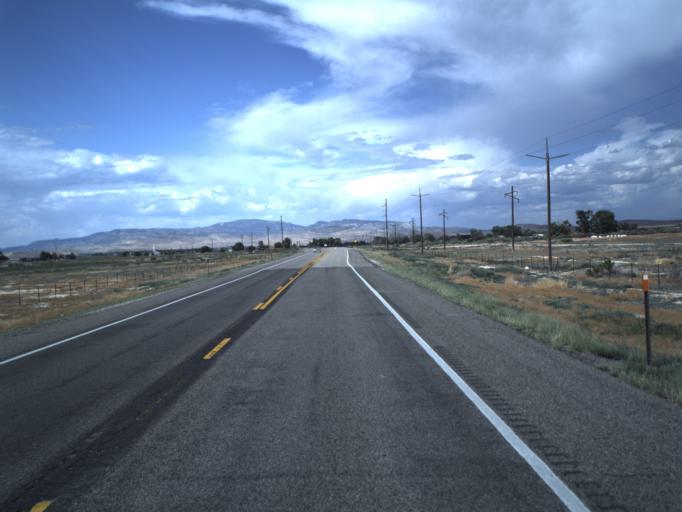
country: US
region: Utah
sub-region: Sanpete County
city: Centerfield
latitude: 39.0414
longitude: -111.8264
